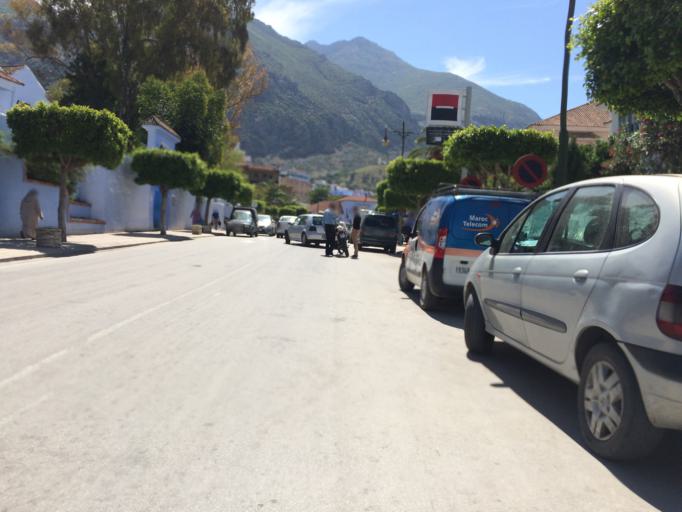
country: MA
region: Tanger-Tetouan
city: Chefchaouene
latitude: 35.1684
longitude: -5.2664
